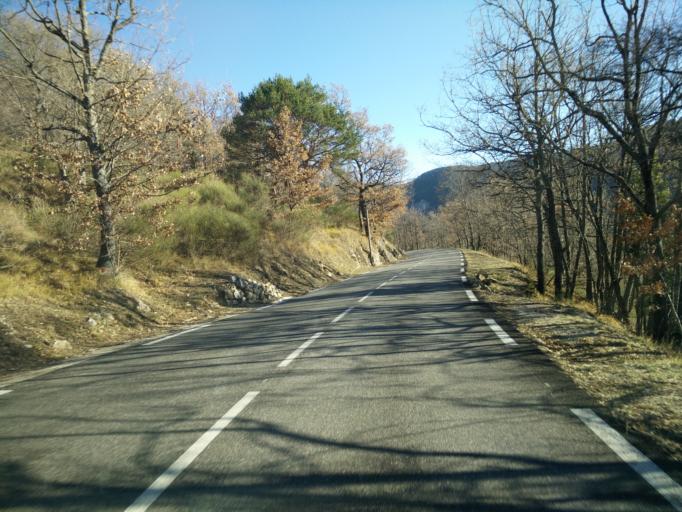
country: FR
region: Provence-Alpes-Cote d'Azur
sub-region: Departement des Alpes-Maritimes
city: Saint-Vallier-de-Thiey
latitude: 43.7177
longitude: 6.8365
